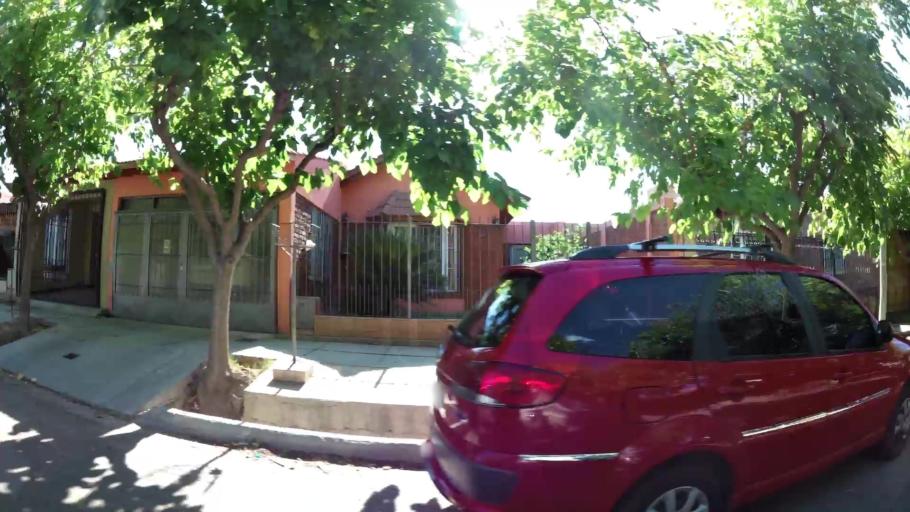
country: AR
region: Mendoza
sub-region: Departamento de Godoy Cruz
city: Godoy Cruz
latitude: -32.9429
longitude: -68.8056
